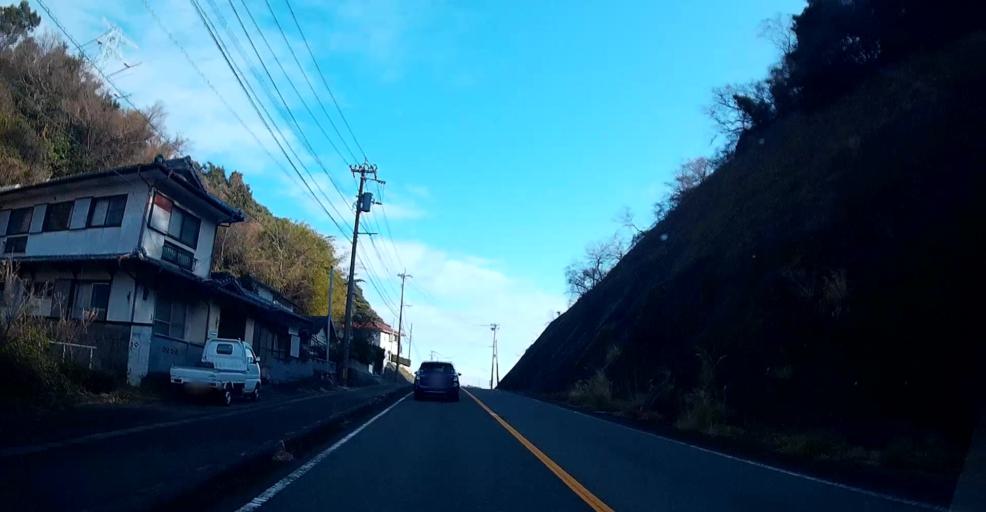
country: JP
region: Kumamoto
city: Yatsushiro
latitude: 32.5175
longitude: 130.4545
